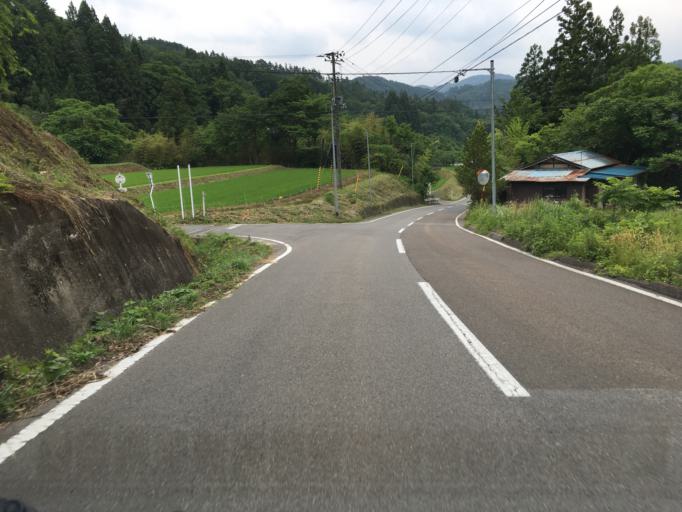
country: JP
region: Fukushima
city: Yanagawamachi-saiwaicho
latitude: 37.7406
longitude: 140.6376
